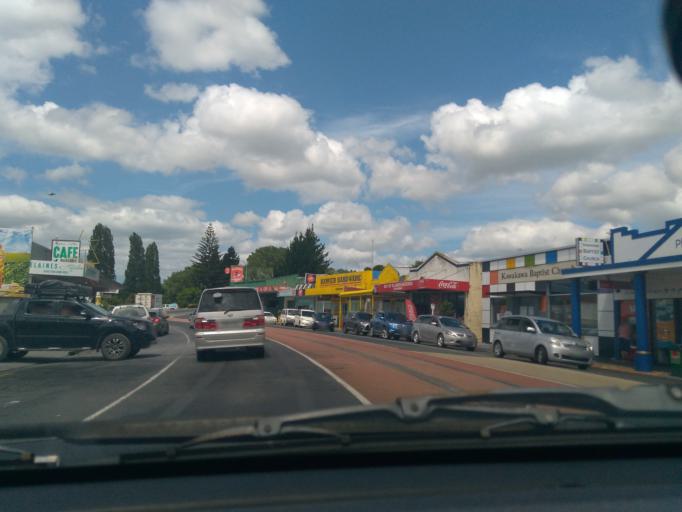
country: NZ
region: Northland
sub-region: Far North District
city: Kawakawa
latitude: -35.3801
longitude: 174.0674
